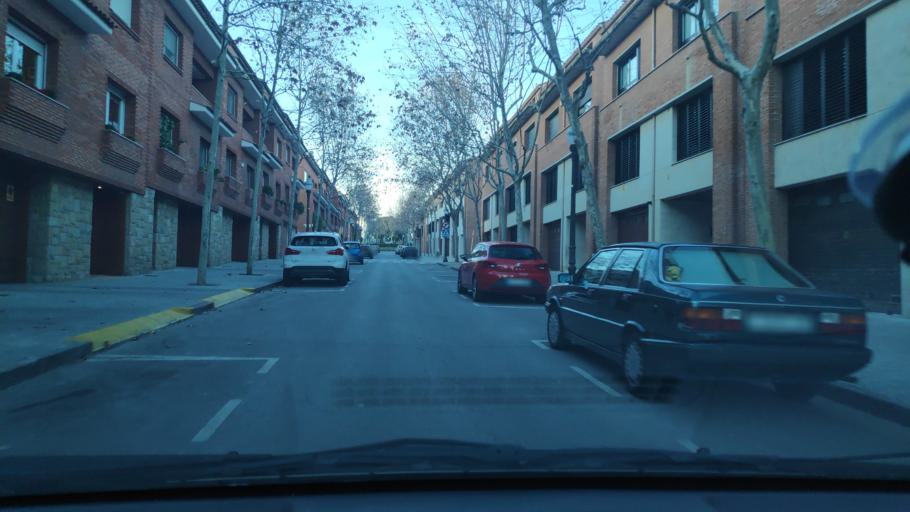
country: ES
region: Catalonia
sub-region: Provincia de Barcelona
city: Sant Quirze del Valles
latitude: 41.5333
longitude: 2.0842
